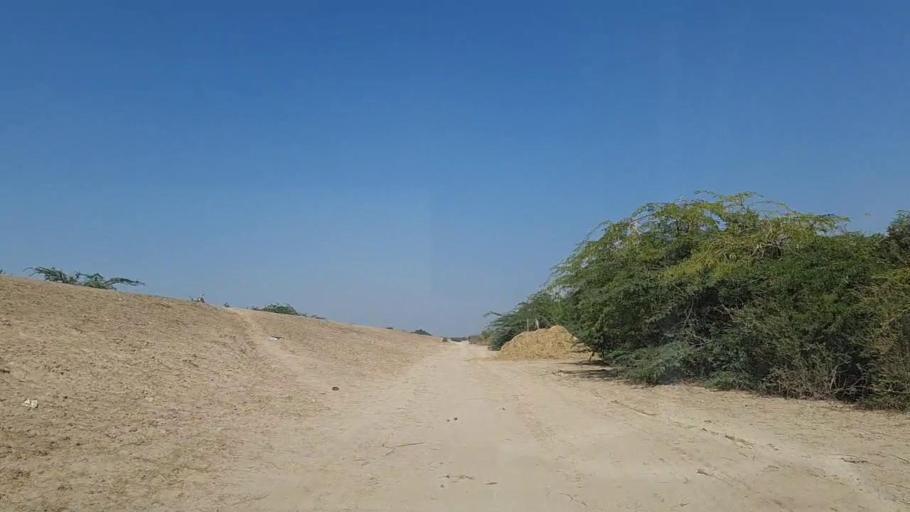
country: PK
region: Sindh
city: Chuhar Jamali
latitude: 24.4750
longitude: 68.0097
